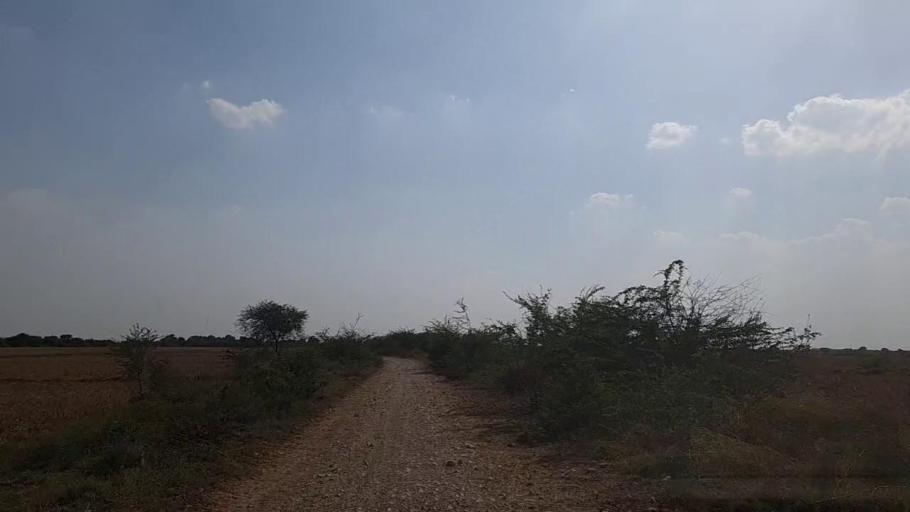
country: PK
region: Sindh
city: Jati
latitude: 24.4827
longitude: 68.3410
